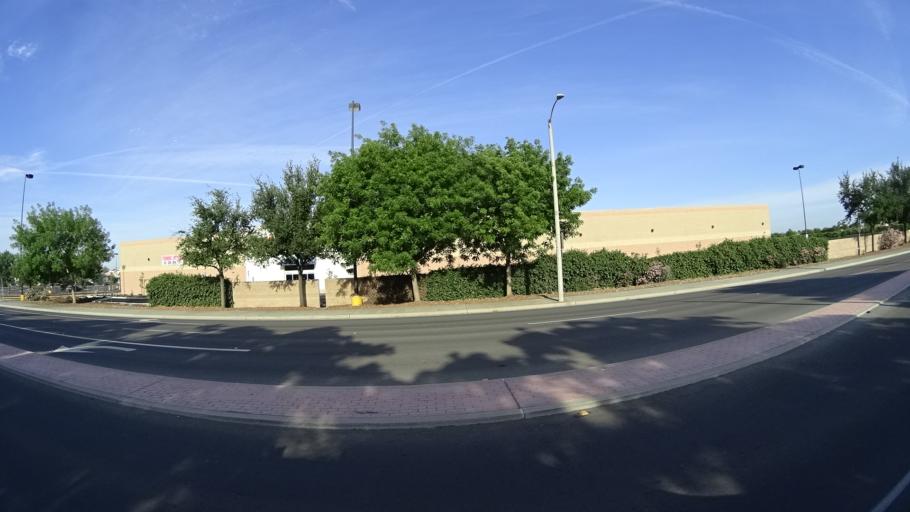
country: US
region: California
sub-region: Kings County
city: Hanford
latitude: 36.3303
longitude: -119.6729
